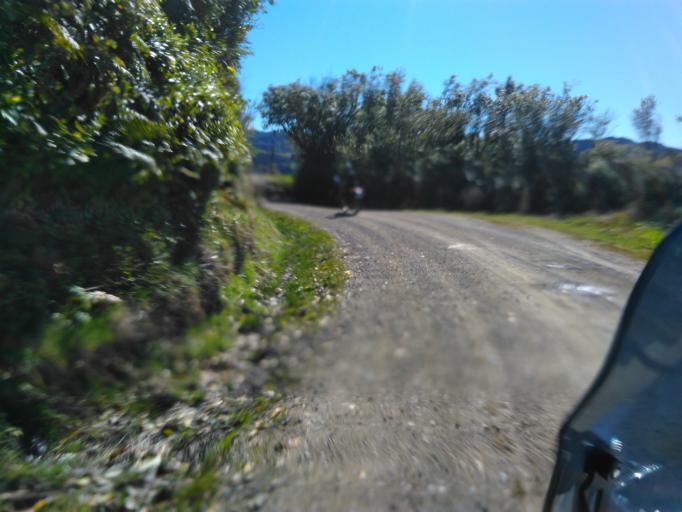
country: NZ
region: Bay of Plenty
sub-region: Opotiki District
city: Opotiki
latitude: -38.3567
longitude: 177.5895
